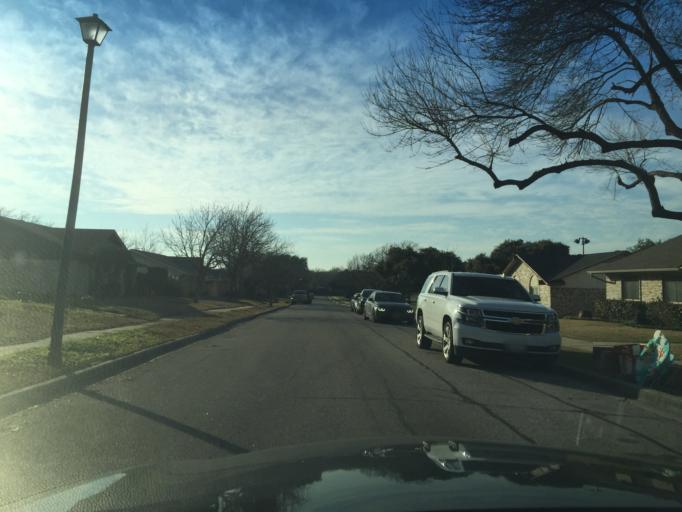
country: US
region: Texas
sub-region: Dallas County
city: Carrollton
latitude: 32.9890
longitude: -96.8811
